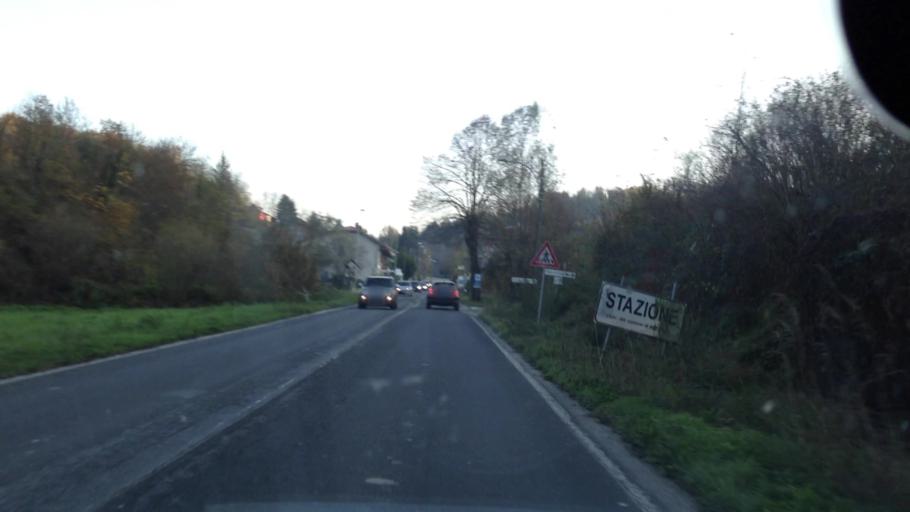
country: IT
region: Piedmont
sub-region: Provincia di Torino
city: Brozolo
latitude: 45.1235
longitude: 8.0578
